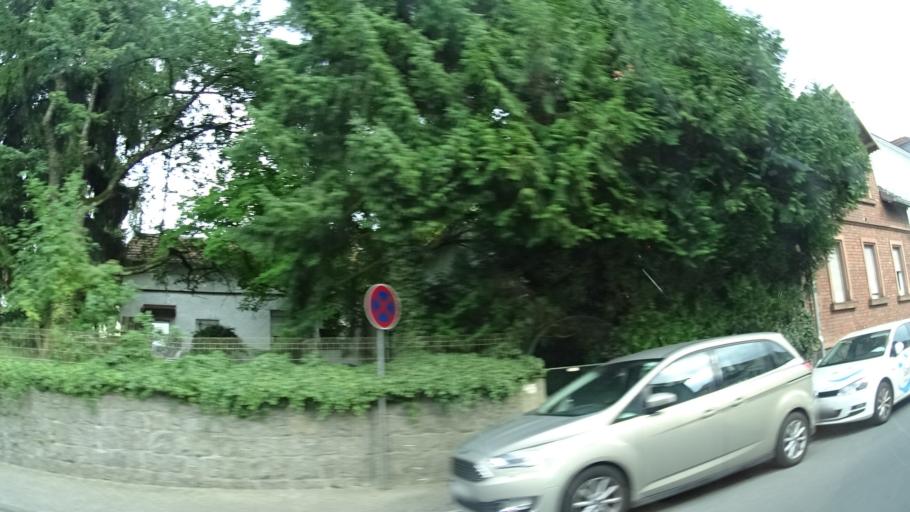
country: DE
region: Hesse
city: Ober-Ramstadt
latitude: 49.8271
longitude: 8.7032
